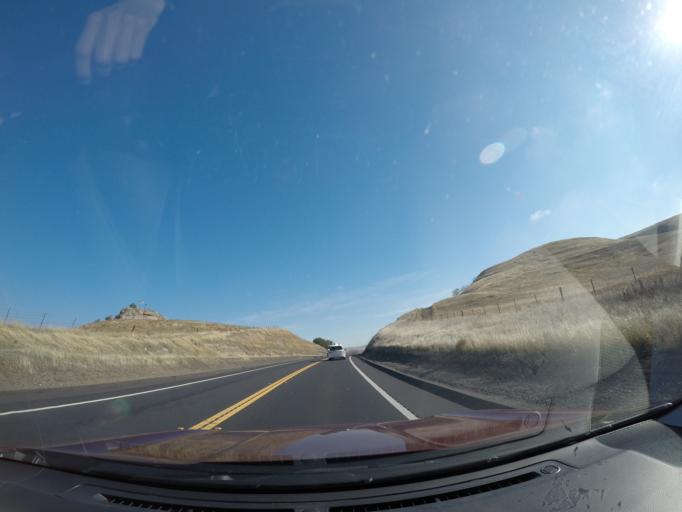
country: US
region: California
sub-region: Stanislaus County
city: East Oakdale
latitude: 37.8067
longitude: -120.6948
